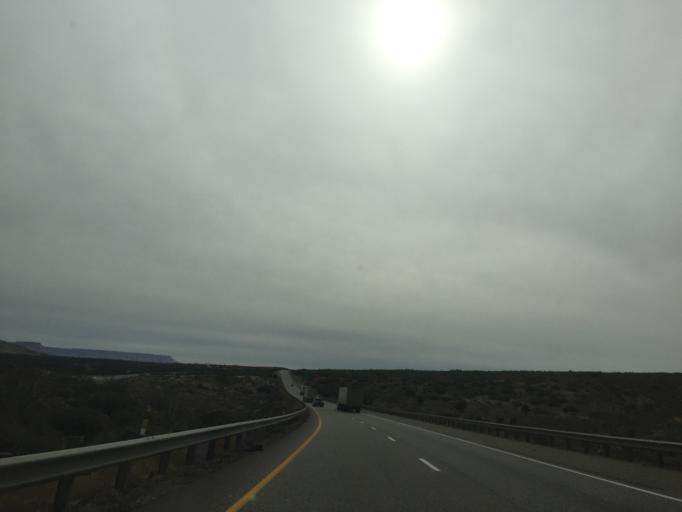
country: US
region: Utah
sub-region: Washington County
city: Toquerville
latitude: 37.3056
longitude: -113.2989
